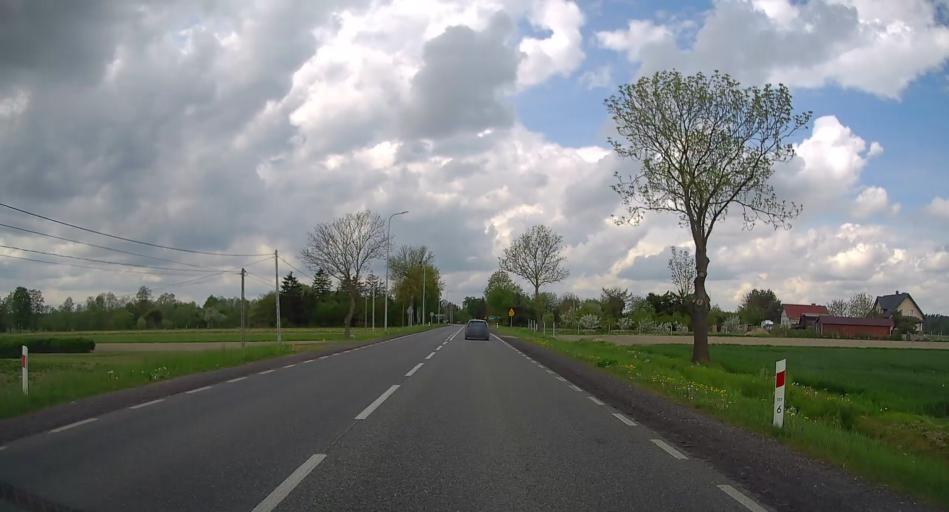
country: PL
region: Masovian Voivodeship
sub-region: Powiat plonski
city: Zaluski
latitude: 52.4464
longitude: 20.5064
